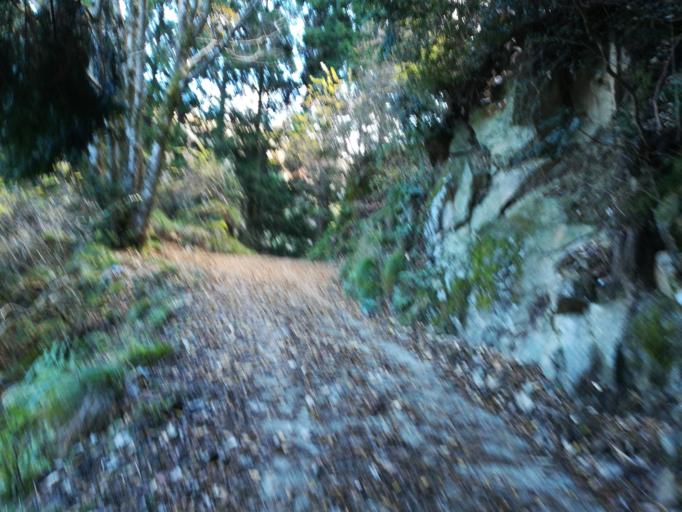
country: JP
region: Kyoto
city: Kameoka
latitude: 34.9832
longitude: 135.6272
